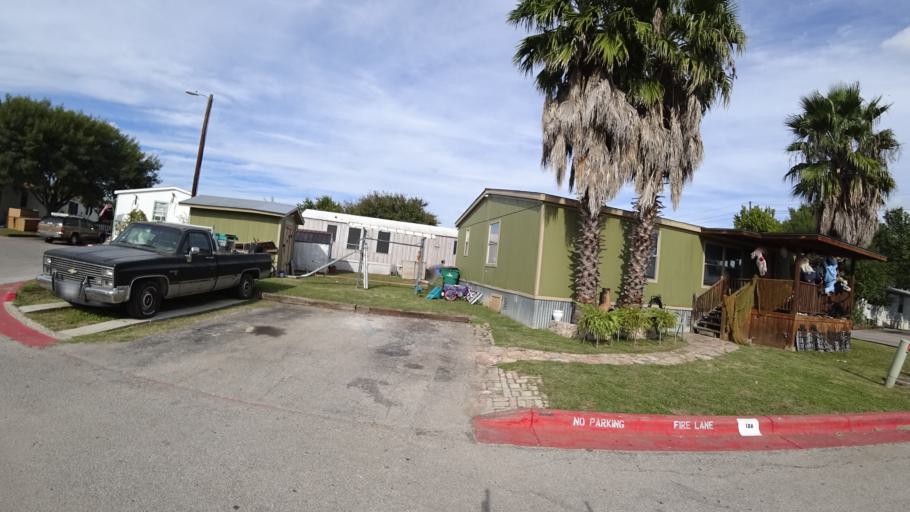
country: US
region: Texas
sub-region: Travis County
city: Onion Creek
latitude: 30.1969
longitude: -97.7576
